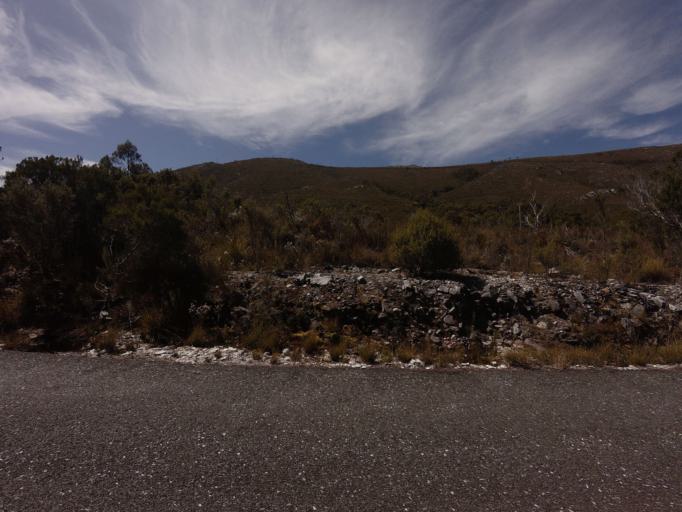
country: AU
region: Tasmania
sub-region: West Coast
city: Queenstown
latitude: -42.7840
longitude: 146.0610
